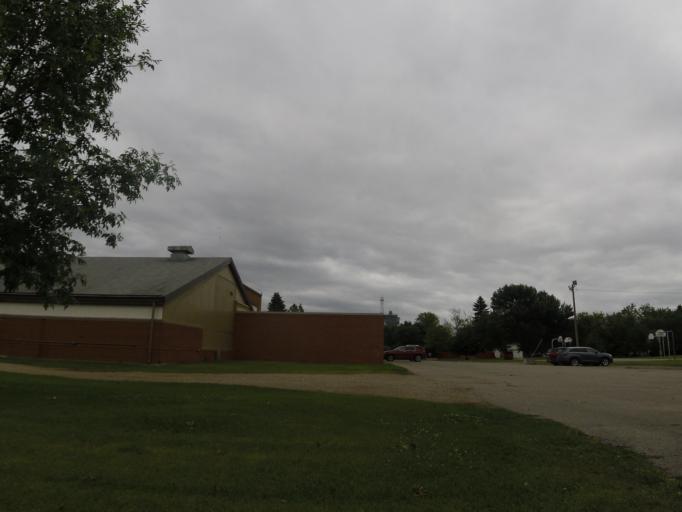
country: US
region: North Dakota
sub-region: Walsh County
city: Grafton
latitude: 48.6188
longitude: -97.4520
